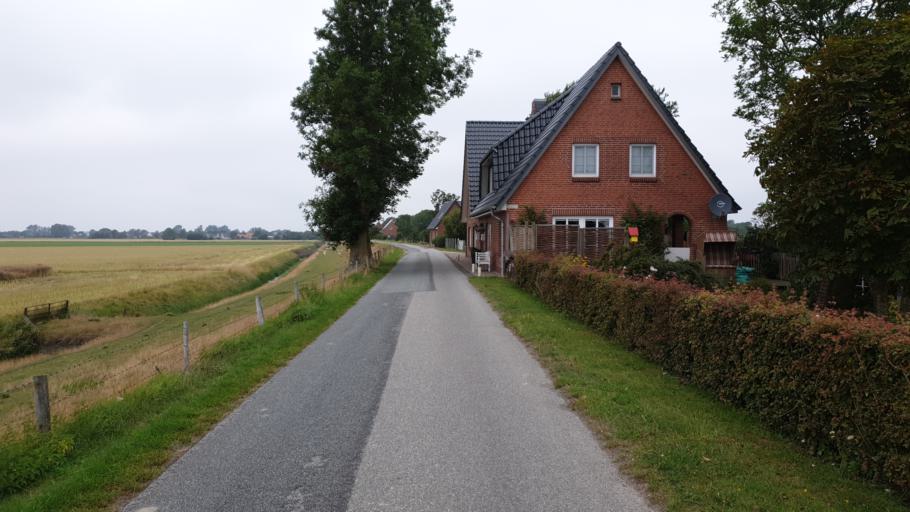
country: DE
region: Schleswig-Holstein
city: Elisabeth-Sophien-Koog
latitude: 54.4826
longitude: 8.8918
